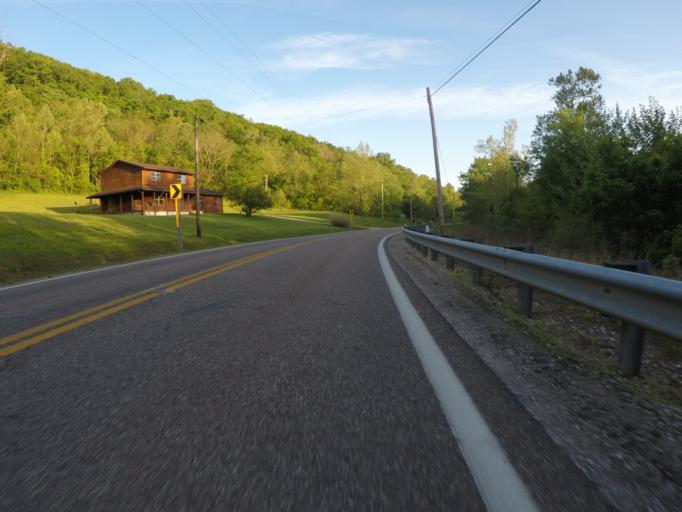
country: US
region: West Virginia
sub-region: Cabell County
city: Huntington
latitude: 38.5003
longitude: -82.4753
